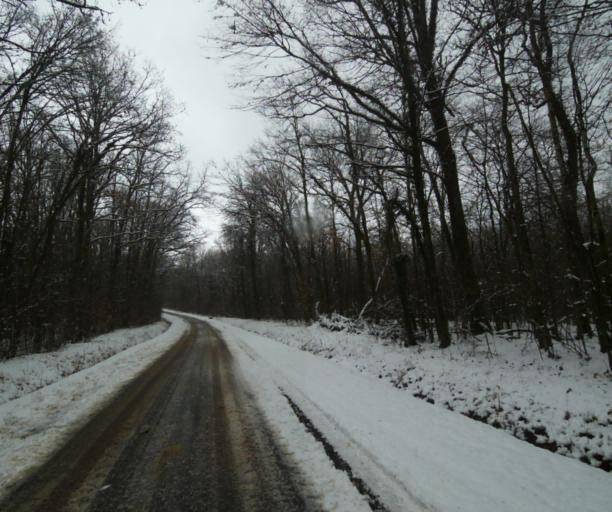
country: FR
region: Champagne-Ardenne
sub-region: Departement de la Haute-Marne
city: Wassy
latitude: 48.4551
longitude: 4.9412
